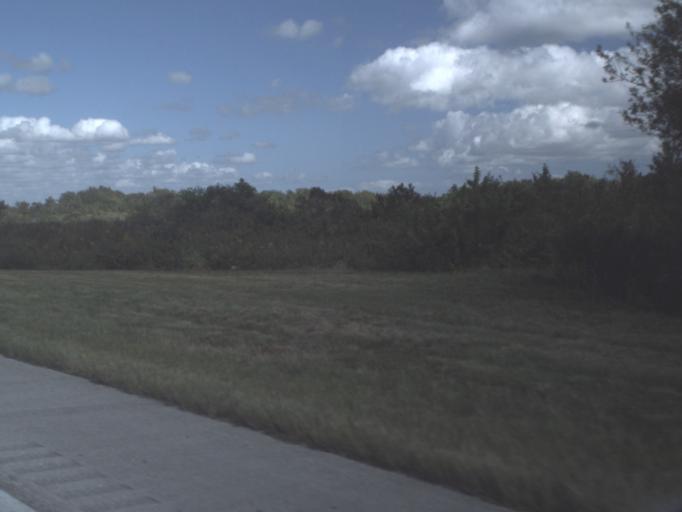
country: US
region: Florida
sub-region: Brevard County
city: Port Saint John
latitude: 28.4247
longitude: -80.8492
